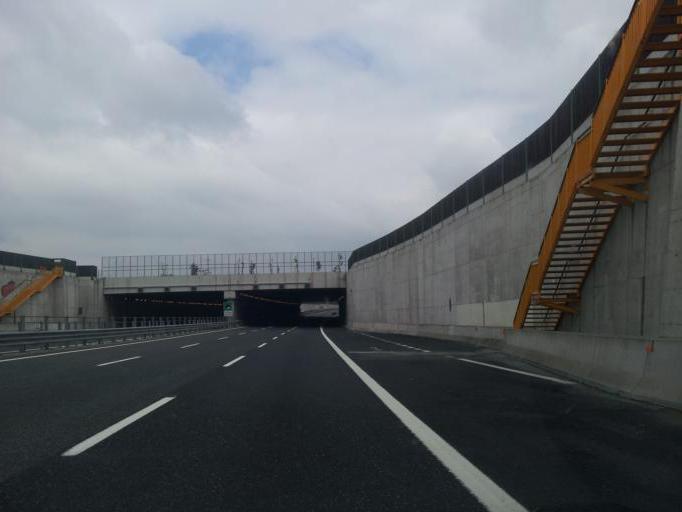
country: IT
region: Veneto
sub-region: Provincia di Venezia
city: Maerne
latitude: 45.5354
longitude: 12.1415
